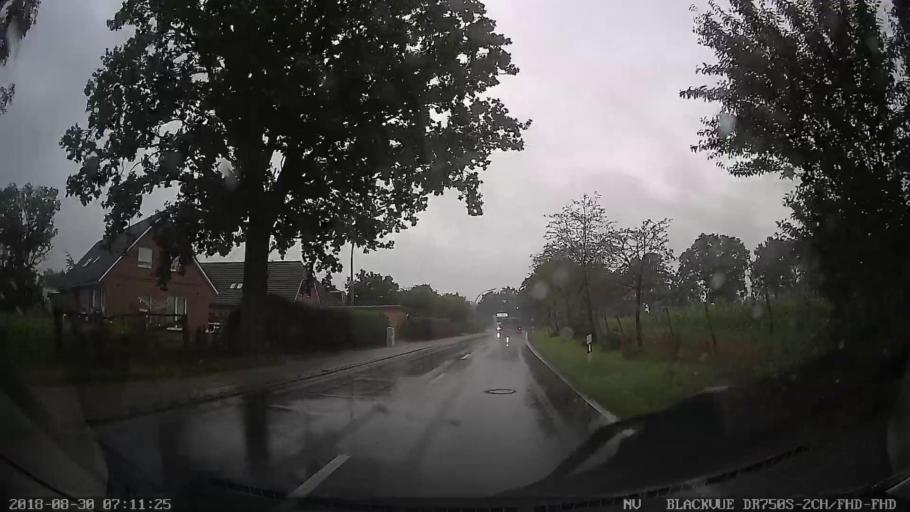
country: DE
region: Schleswig-Holstein
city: Ellerbek
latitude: 53.6454
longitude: 9.8714
